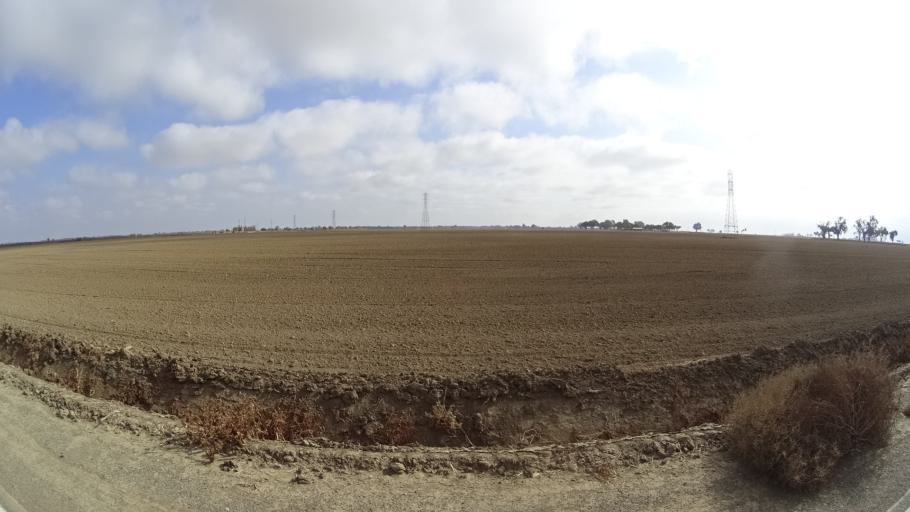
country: US
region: California
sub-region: Yolo County
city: Woodland
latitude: 38.7961
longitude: -121.7747
